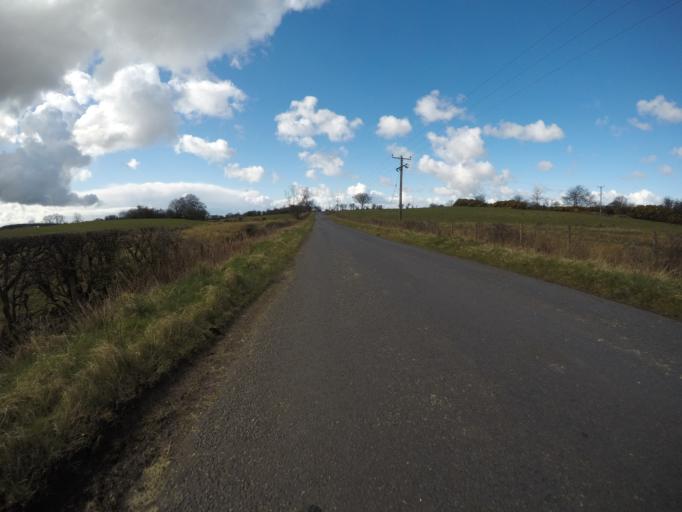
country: GB
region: Scotland
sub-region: North Ayrshire
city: Kilbirnie
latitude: 55.7165
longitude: -4.6817
